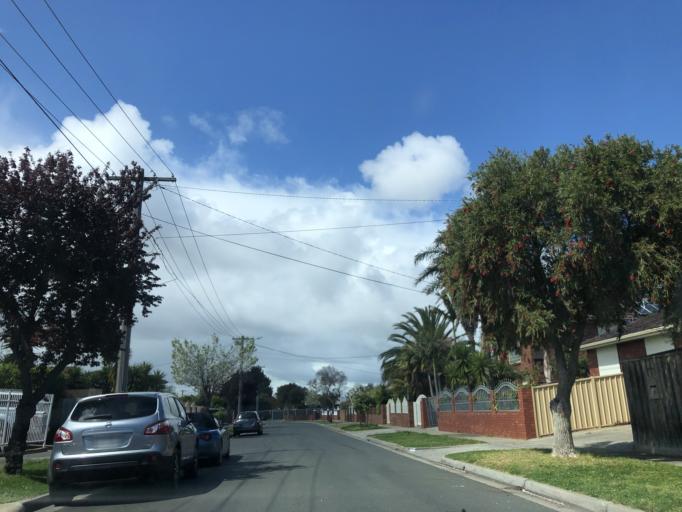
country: AU
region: Victoria
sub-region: Monash
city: Oakleigh South
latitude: -37.9381
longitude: 145.0940
